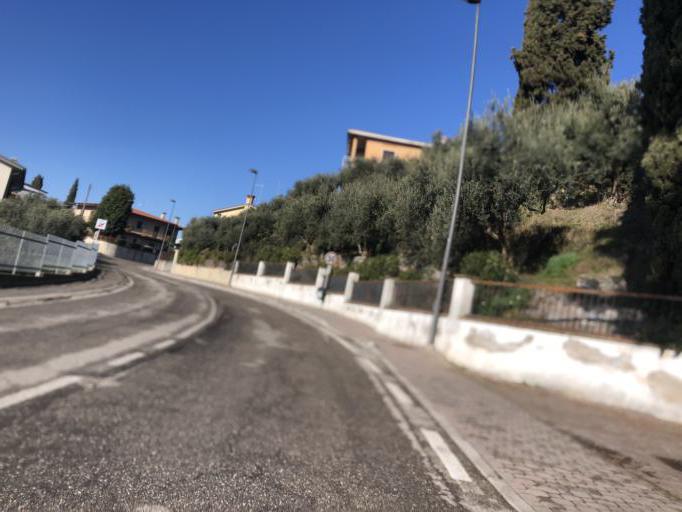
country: IT
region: Veneto
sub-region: Provincia di Verona
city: Sona
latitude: 45.4364
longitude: 10.8282
